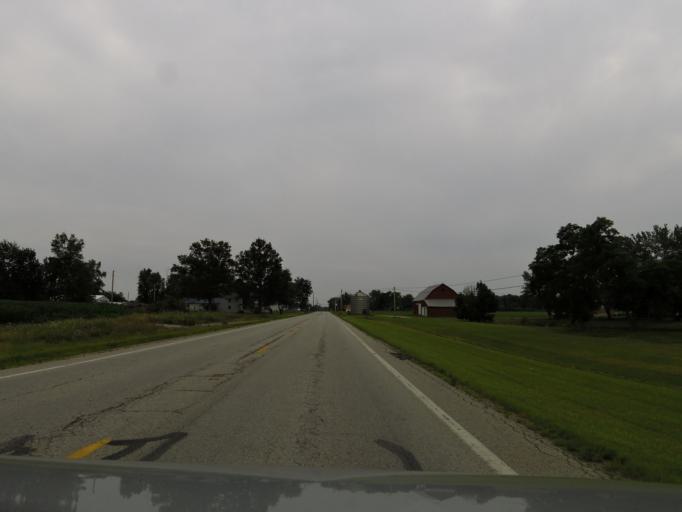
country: US
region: Ohio
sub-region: Brown County
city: Mount Orab
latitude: 39.1225
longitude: -83.9331
